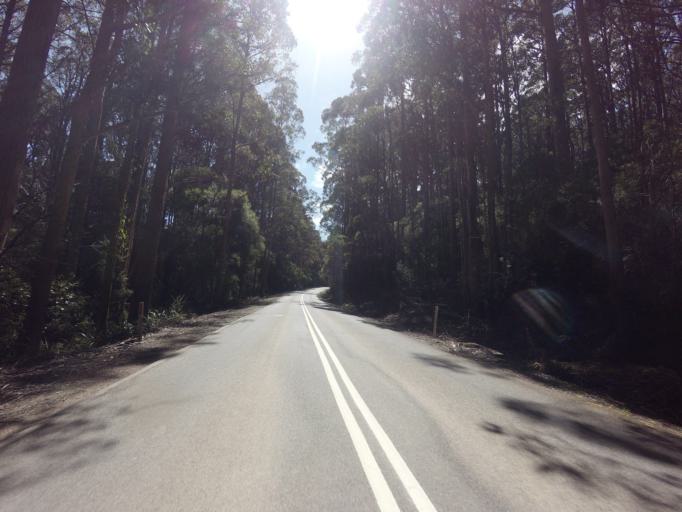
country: AU
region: Tasmania
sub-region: Derwent Valley
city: New Norfolk
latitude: -42.7344
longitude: 146.6656
